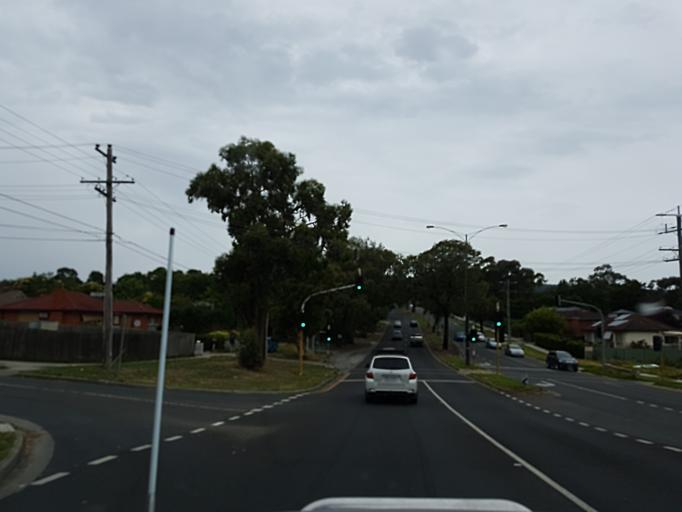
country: AU
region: Victoria
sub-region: Knox
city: Boronia
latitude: -37.8611
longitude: 145.2734
